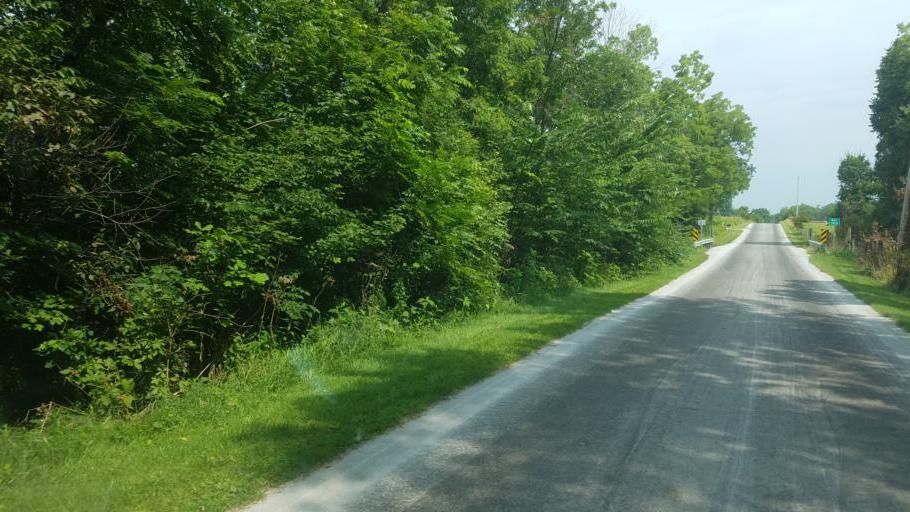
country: US
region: Ohio
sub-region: Hardin County
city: Kenton
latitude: 40.6143
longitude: -83.5276
